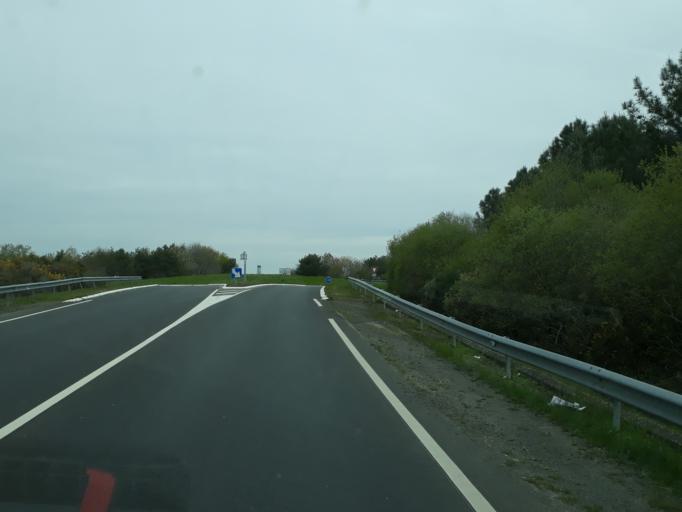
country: FR
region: Brittany
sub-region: Departement du Morbihan
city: Surzur
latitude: 47.6094
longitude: -2.6145
